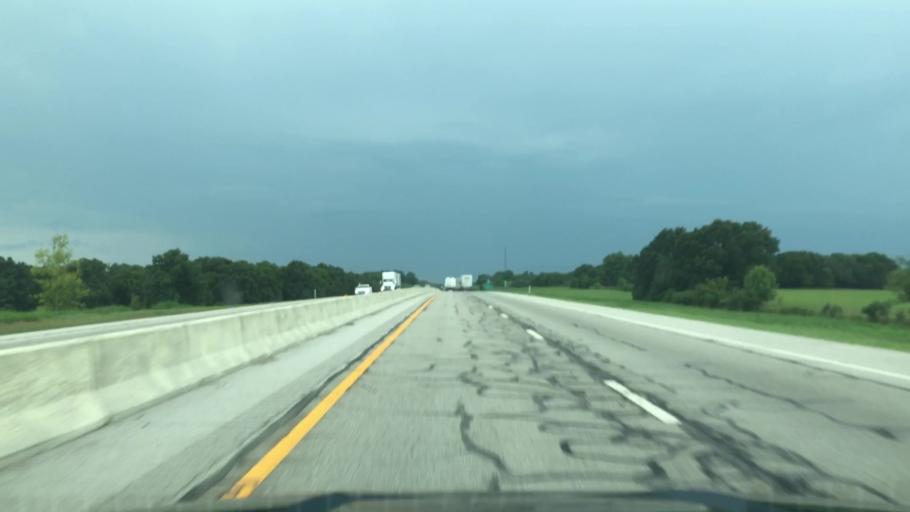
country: US
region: Oklahoma
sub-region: Rogers County
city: Bushyhead
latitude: 36.4316
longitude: -95.3873
